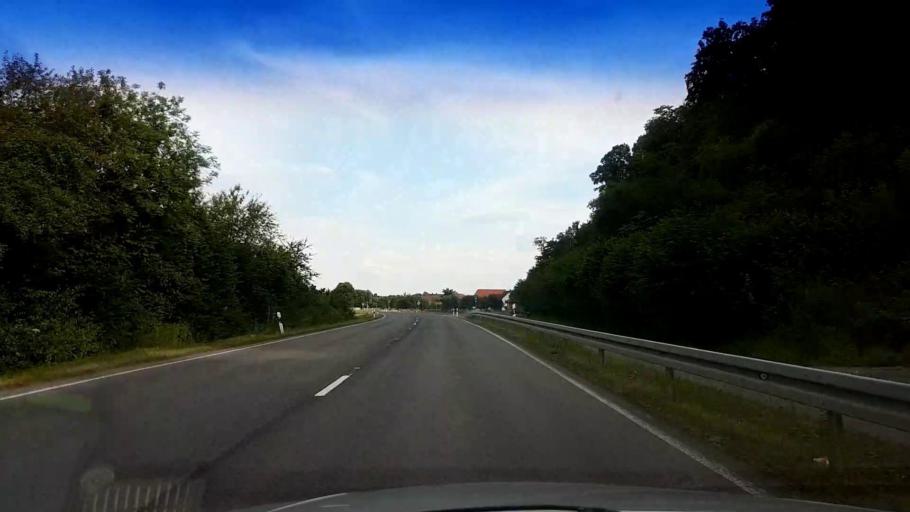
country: DE
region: Bavaria
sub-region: Regierungsbezirk Unterfranken
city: Stettfeld
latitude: 49.9612
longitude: 10.7106
